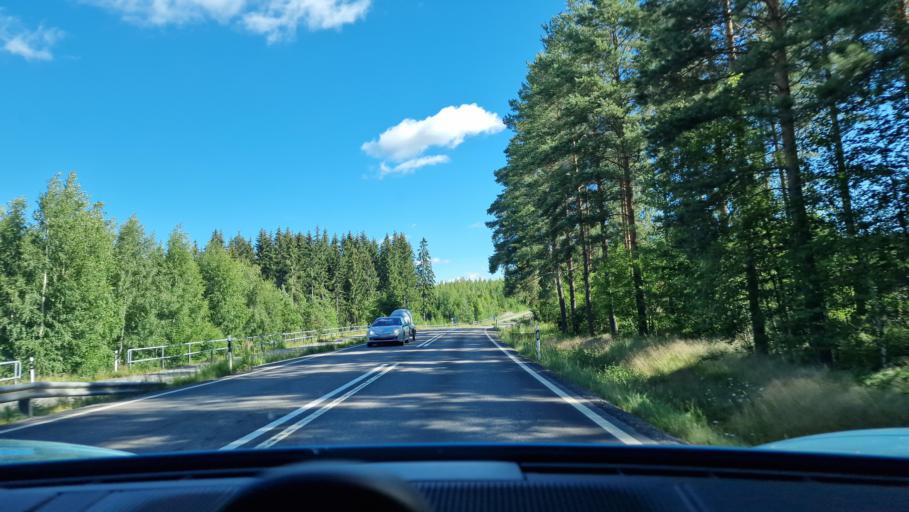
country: FI
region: Pirkanmaa
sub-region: Tampere
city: Kangasala
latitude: 61.4697
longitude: 24.1299
